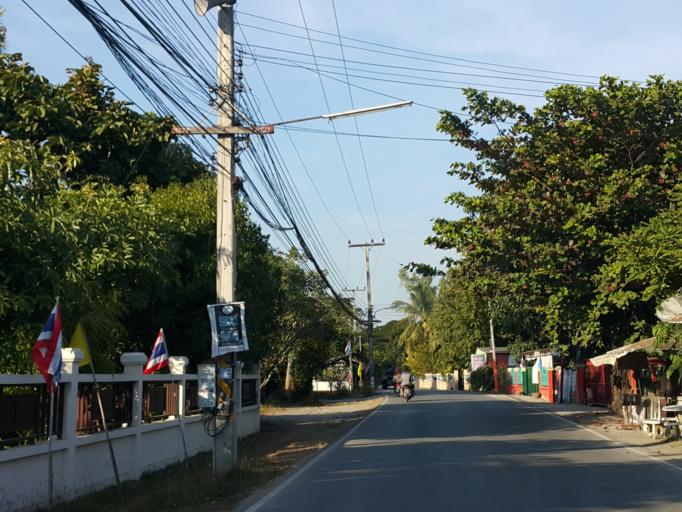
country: TH
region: Chiang Mai
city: San Sai
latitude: 18.7958
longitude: 99.0593
